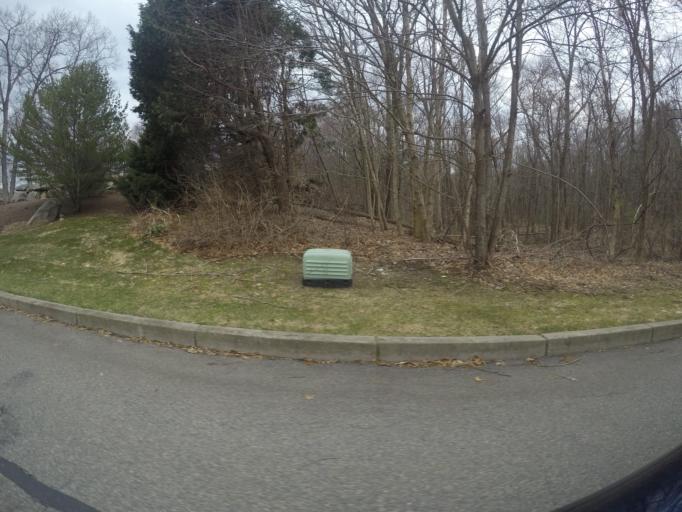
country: US
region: Massachusetts
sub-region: Norfolk County
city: Stoughton
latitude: 42.0809
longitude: -71.1030
